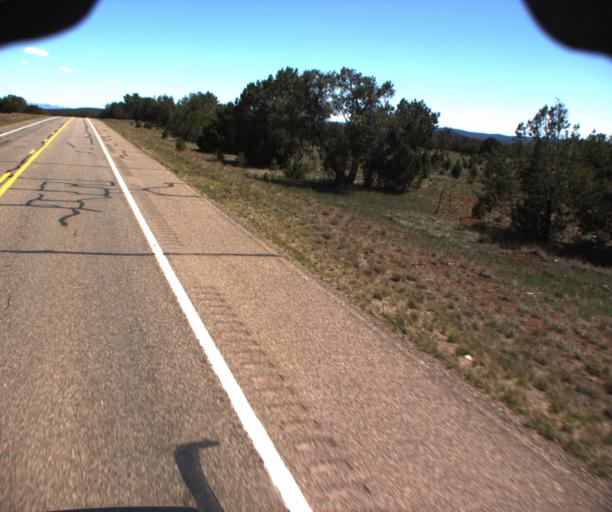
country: US
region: Arizona
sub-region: Coconino County
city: Williams
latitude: 35.1659
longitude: -112.4587
